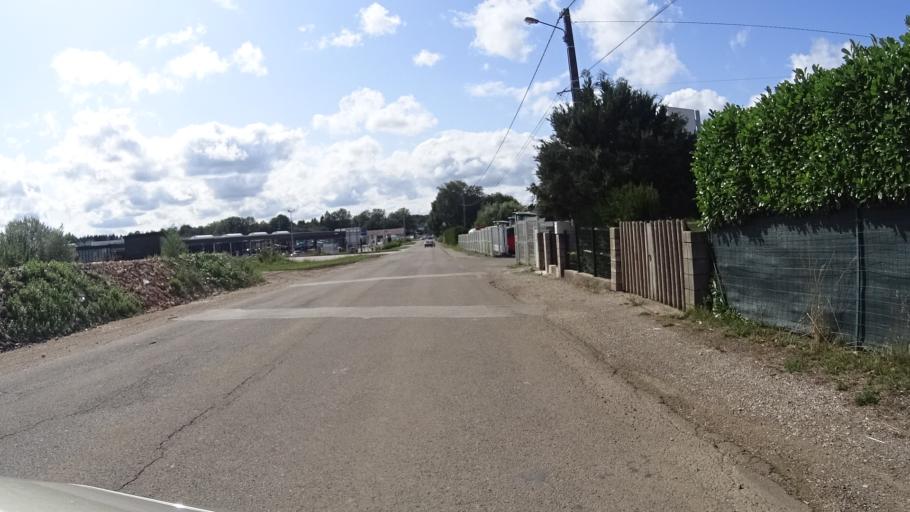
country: FR
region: Franche-Comte
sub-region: Departement du Doubs
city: Saone
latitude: 47.2084
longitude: 6.1056
